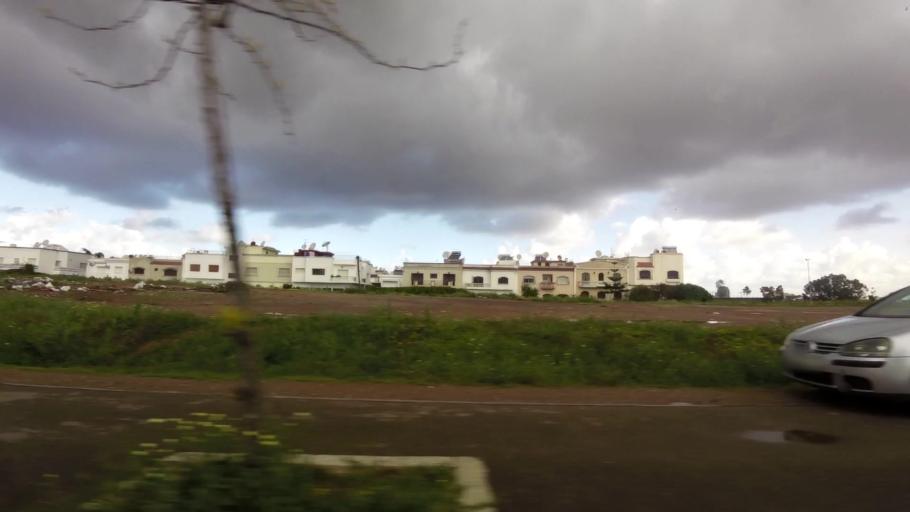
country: MA
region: Grand Casablanca
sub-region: Casablanca
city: Casablanca
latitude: 33.5459
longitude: -7.6572
